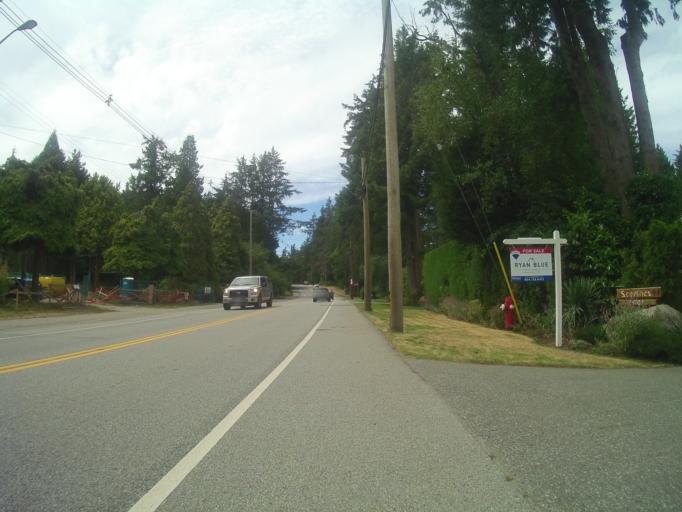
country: CA
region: British Columbia
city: Surrey
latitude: 49.0566
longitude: -122.8587
